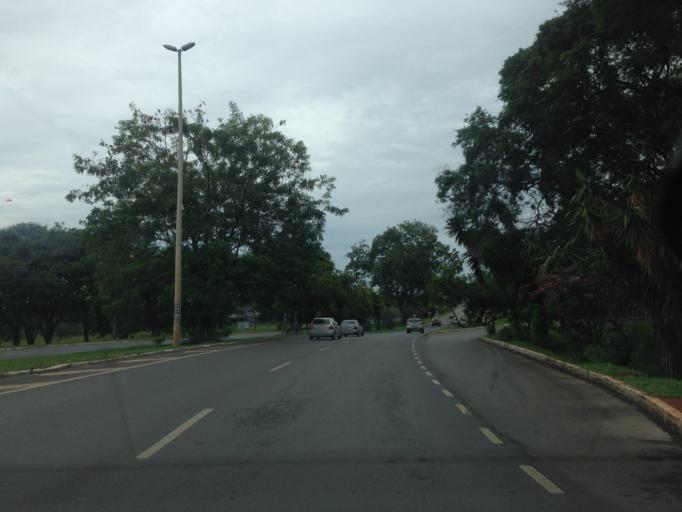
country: BR
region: Federal District
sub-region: Brasilia
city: Brasilia
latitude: -15.8029
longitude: -47.8780
